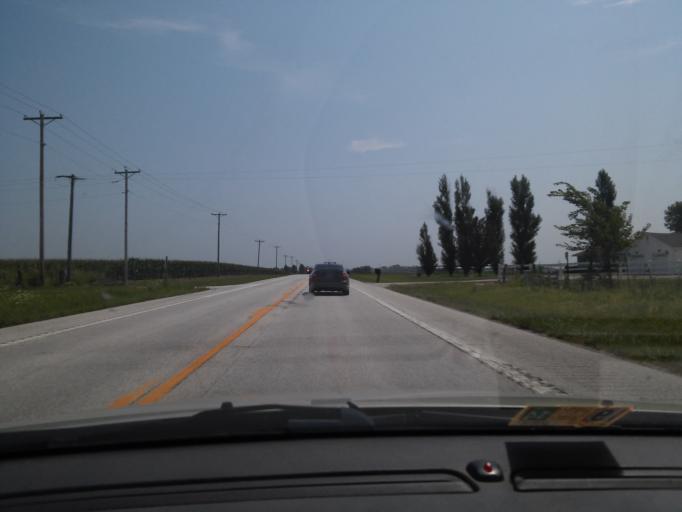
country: US
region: Missouri
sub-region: Pike County
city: Bowling Green
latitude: 39.3444
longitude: -91.2565
